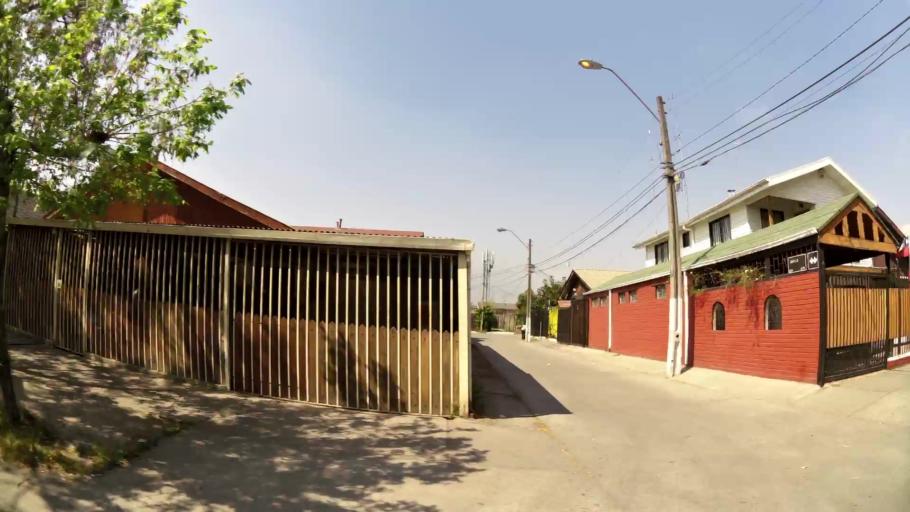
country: CL
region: Santiago Metropolitan
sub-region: Provincia de Santiago
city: La Pintana
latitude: -33.5484
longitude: -70.5959
